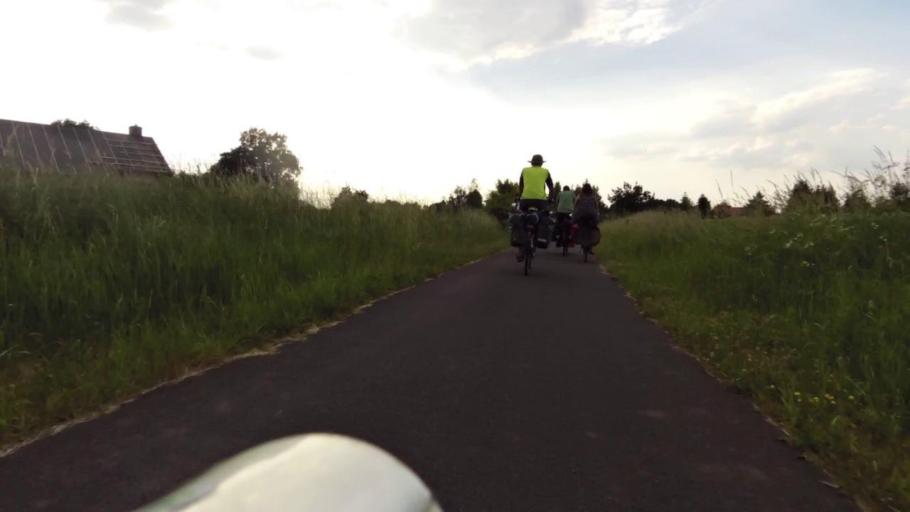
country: PL
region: Kujawsko-Pomorskie
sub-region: Powiat torunski
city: Lubianka
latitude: 53.1109
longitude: 18.4755
